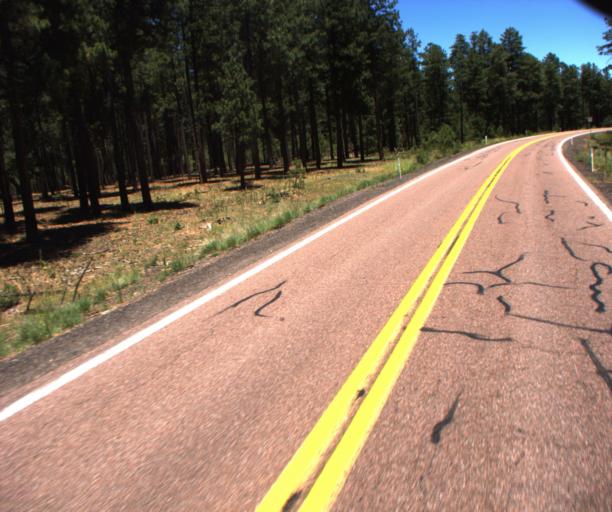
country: US
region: Arizona
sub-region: Gila County
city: Pine
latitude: 34.4523
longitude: -111.4169
